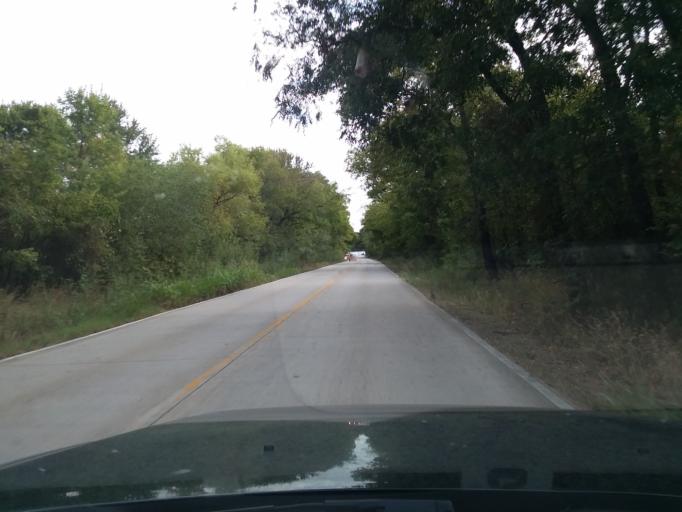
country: US
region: Texas
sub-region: Denton County
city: Copper Canyon
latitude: 33.1264
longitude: -97.1072
